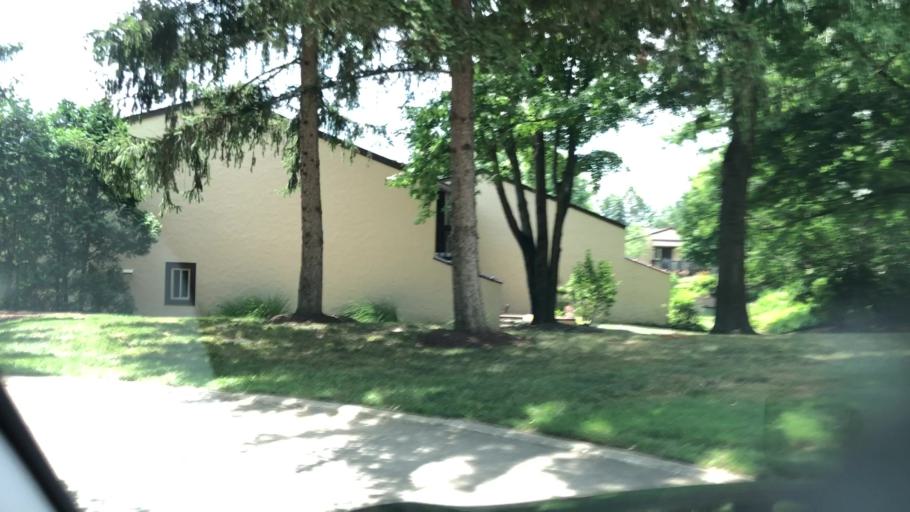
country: US
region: Ohio
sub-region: Summit County
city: Fairlawn
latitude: 41.1306
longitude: -81.6275
